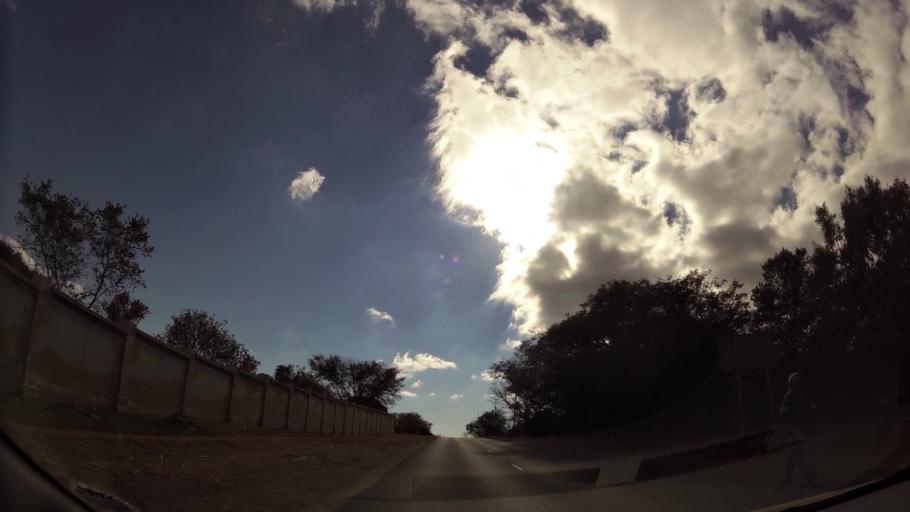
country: ZA
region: Gauteng
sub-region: West Rand District Municipality
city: Muldersdriseloop
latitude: -26.0836
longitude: 27.8546
